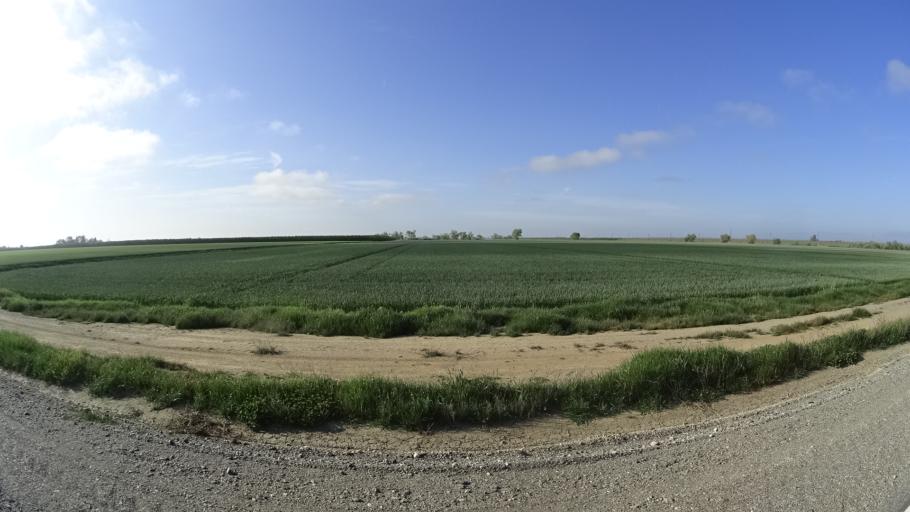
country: US
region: California
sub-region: Glenn County
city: Willows
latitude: 39.5825
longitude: -122.1704
